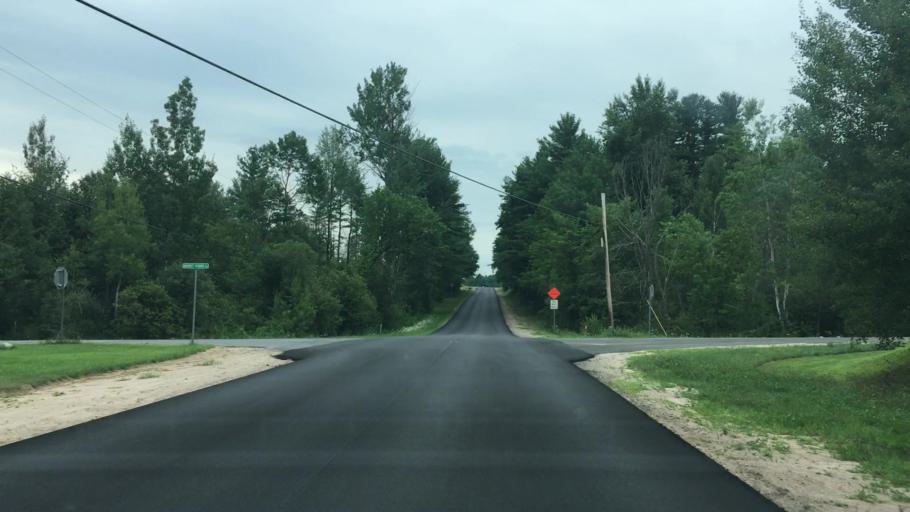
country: US
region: New York
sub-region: Clinton County
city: Peru
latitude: 44.5760
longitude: -73.5699
